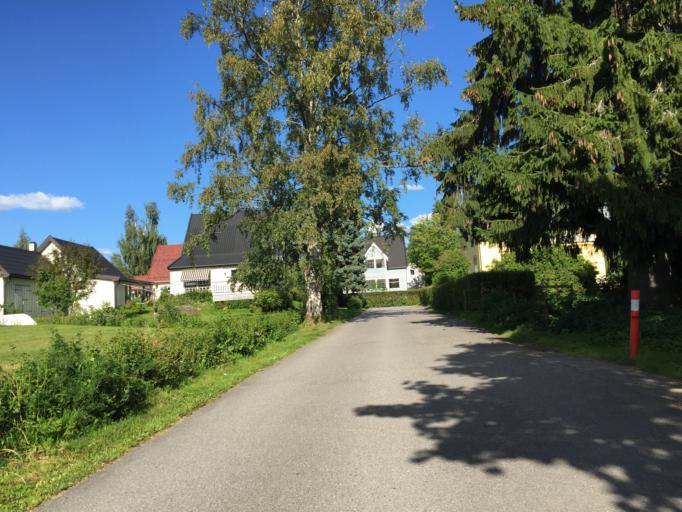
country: NO
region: Hedmark
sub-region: Kongsvinger
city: Kongsvinger
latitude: 60.1930
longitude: 11.9962
